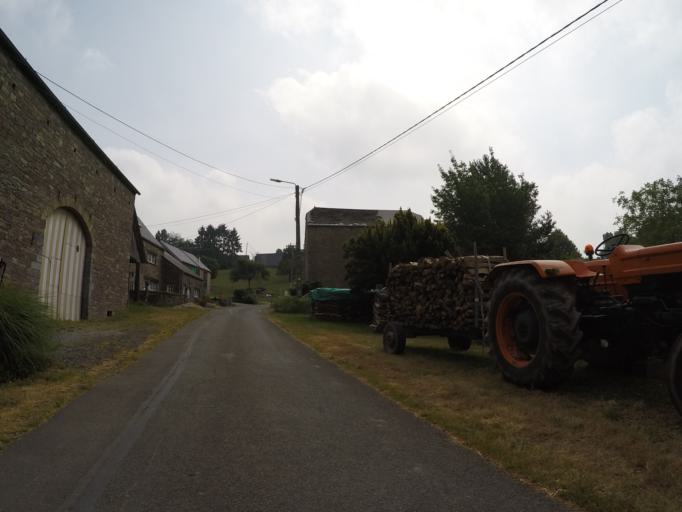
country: BE
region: Wallonia
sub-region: Province de Namur
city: Assesse
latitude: 50.3404
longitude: 4.9710
